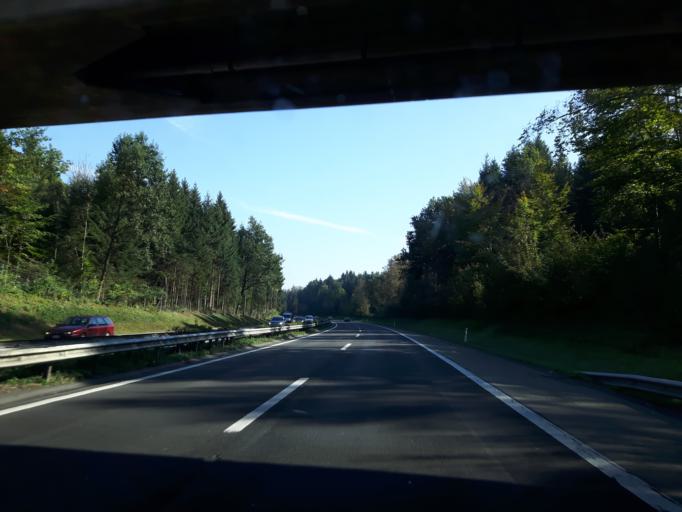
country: CH
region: Lucerne
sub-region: Sursee District
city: Knutwil
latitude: 47.1816
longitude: 8.0838
